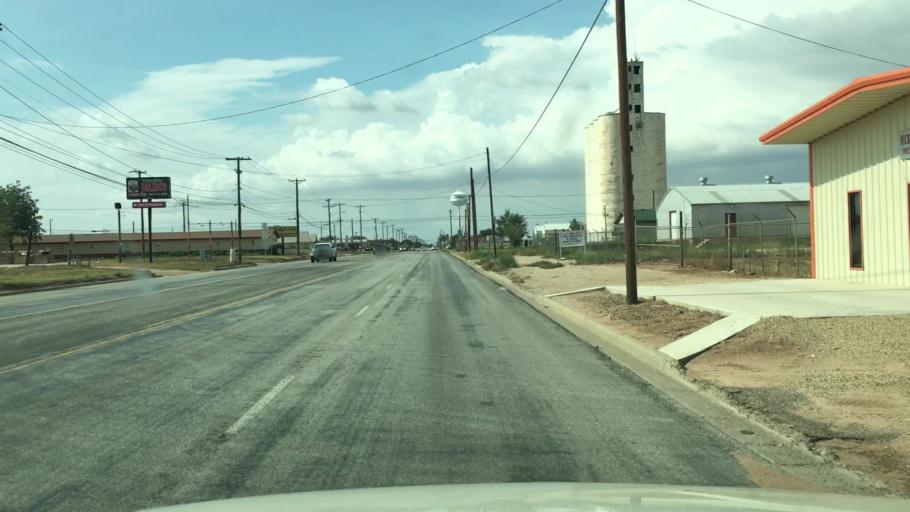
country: US
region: Texas
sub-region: Dawson County
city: Lamesa
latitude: 32.7247
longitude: -101.9466
